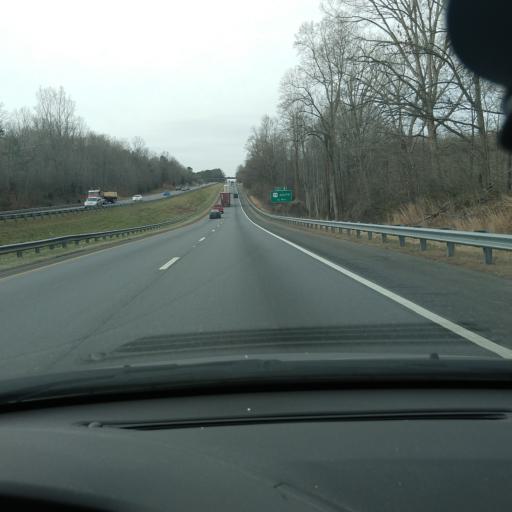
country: US
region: North Carolina
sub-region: Cleveland County
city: White Plains
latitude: 35.1981
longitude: -81.3795
